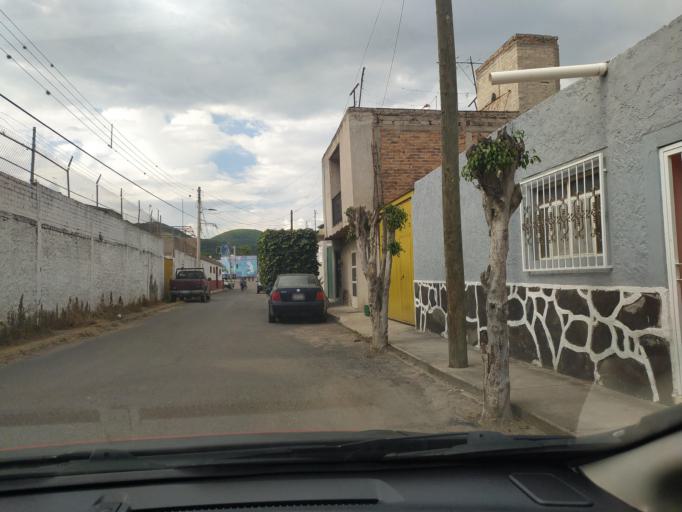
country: MX
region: Jalisco
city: Villa Corona
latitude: 20.4134
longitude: -103.6667
